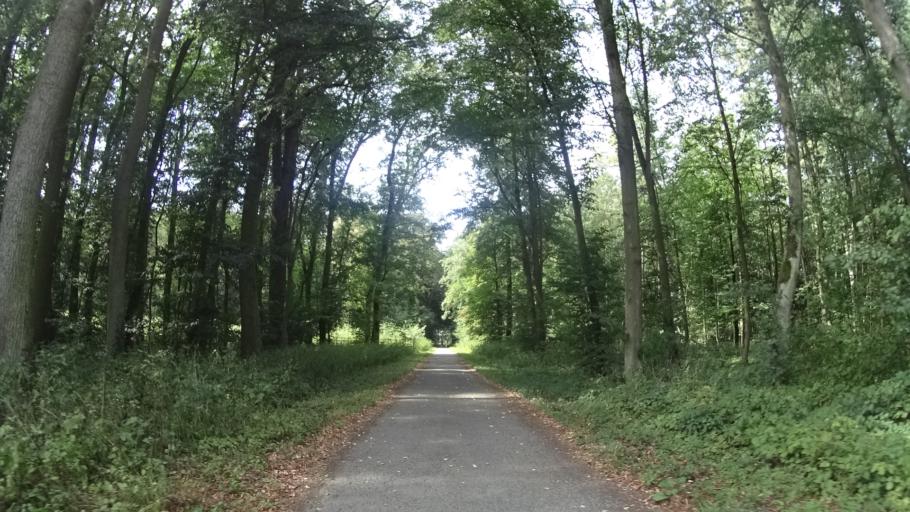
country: CZ
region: Olomoucky
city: Skrben
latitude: 49.6623
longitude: 17.1840
